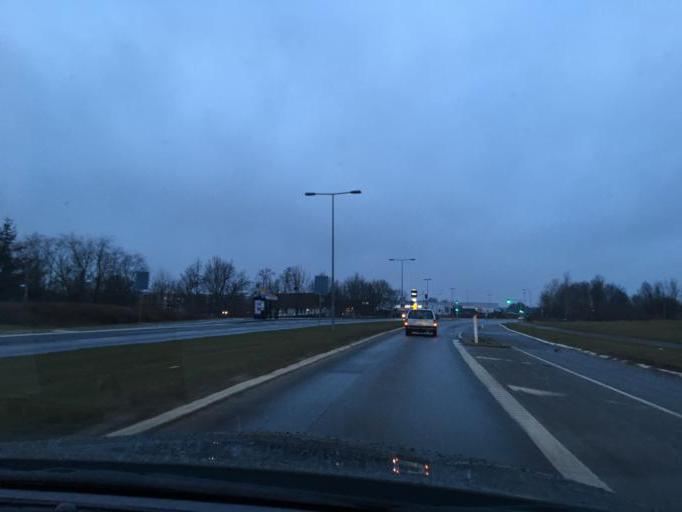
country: DK
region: Capital Region
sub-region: Fredensborg Kommune
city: Kokkedal
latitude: 55.9036
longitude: 12.4779
